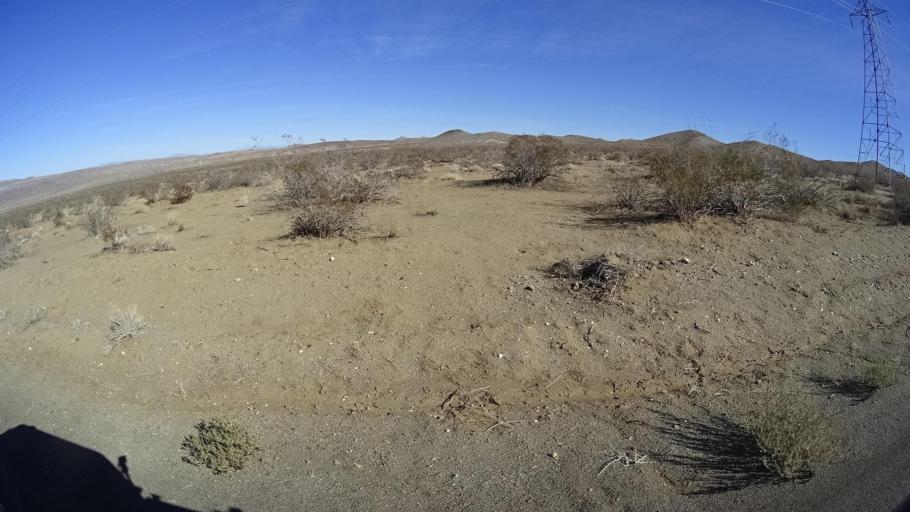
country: US
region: California
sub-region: Kern County
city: Ridgecrest
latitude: 35.3831
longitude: -117.6619
